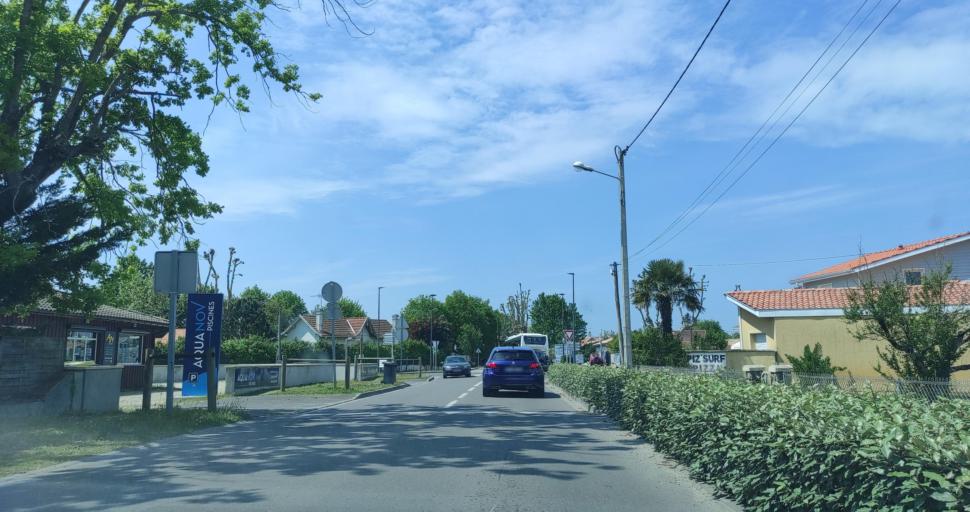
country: FR
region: Aquitaine
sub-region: Departement de la Gironde
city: Ares
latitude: 44.7626
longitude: -1.1316
